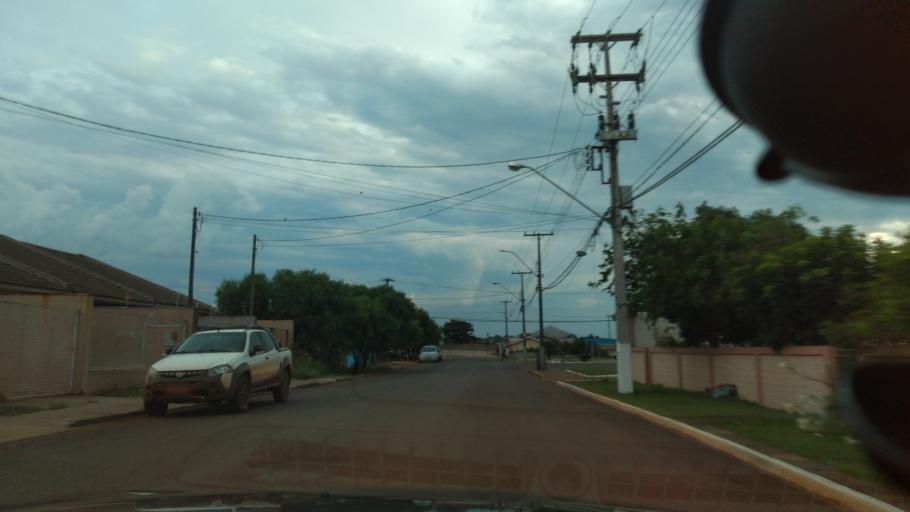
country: BR
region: Parana
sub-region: Guarapuava
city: Guarapuava
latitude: -25.3925
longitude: -51.4924
